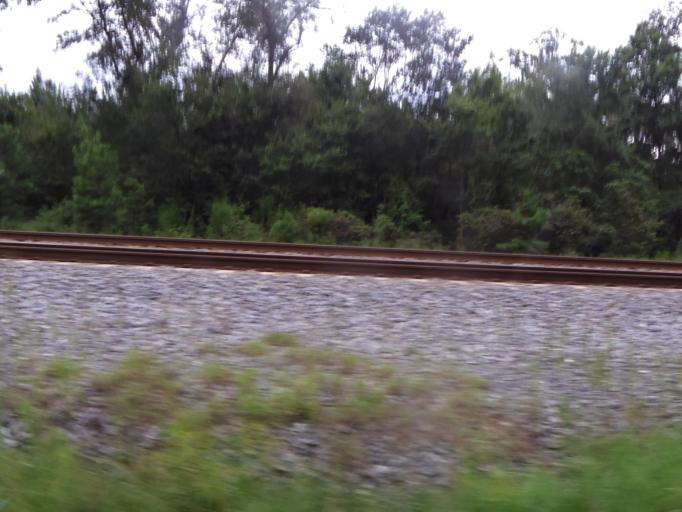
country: US
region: Florida
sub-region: Duval County
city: Baldwin
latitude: 30.3895
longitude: -81.9409
